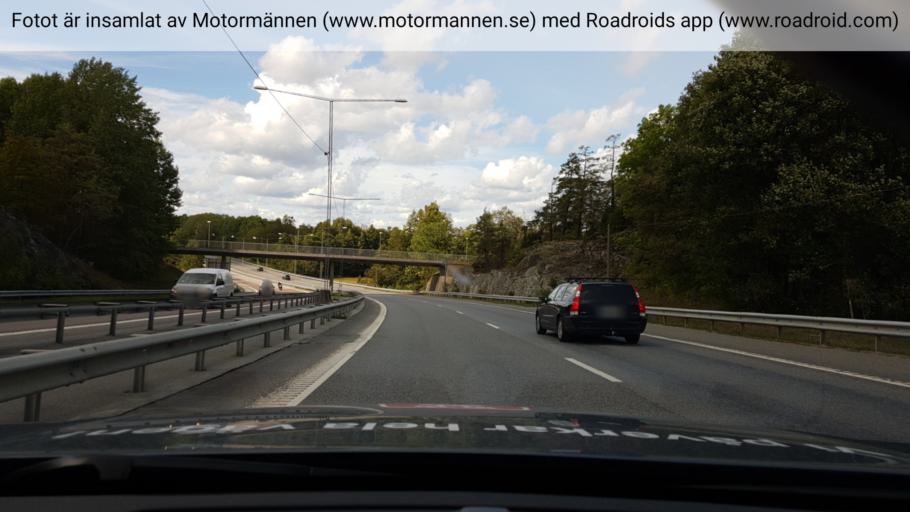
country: SE
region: Stockholm
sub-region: Nacka Kommun
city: Alta
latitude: 59.2551
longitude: 18.1701
